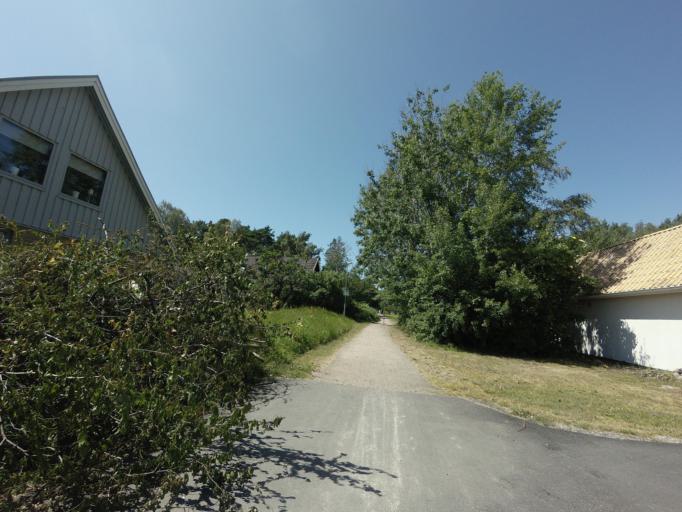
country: SE
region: Skane
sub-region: Vellinge Kommun
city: Skanor med Falsterbo
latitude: 55.4054
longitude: 12.8491
